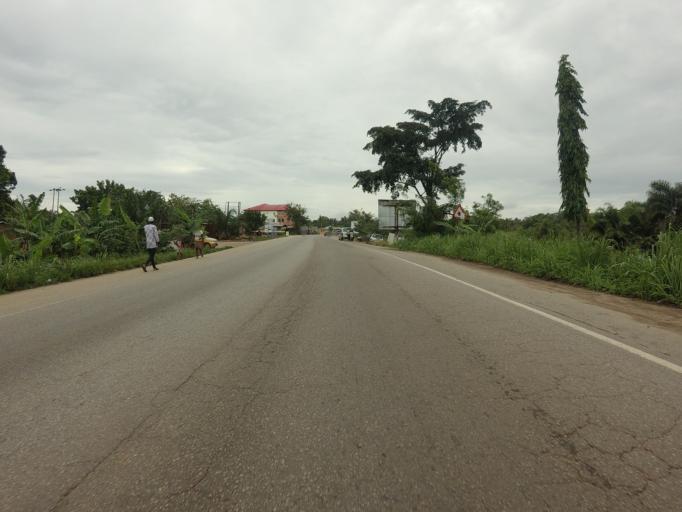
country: GH
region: Eastern
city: Begoro
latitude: 6.3883
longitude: -0.5544
